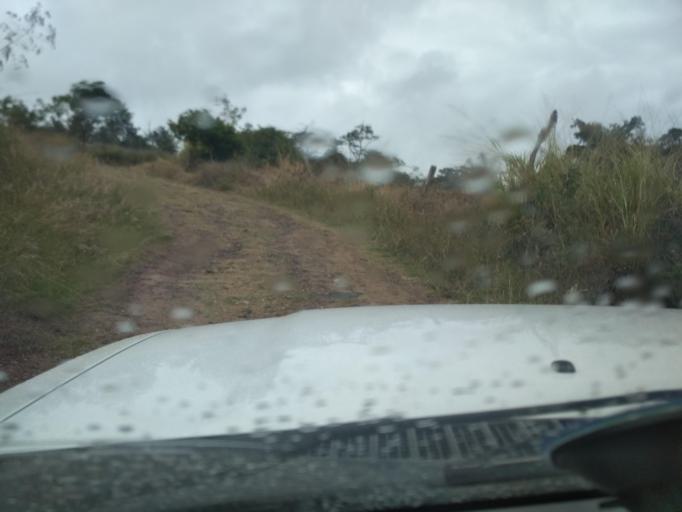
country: MX
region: Veracruz
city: El Castillo
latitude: 19.5355
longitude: -96.8234
